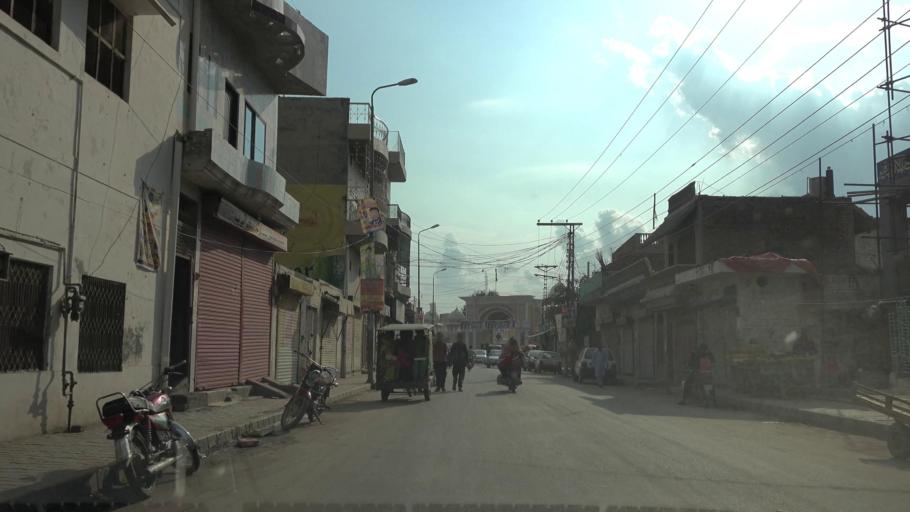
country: PK
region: Punjab
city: Nankana Sahib
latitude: 31.4467
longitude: 73.6988
